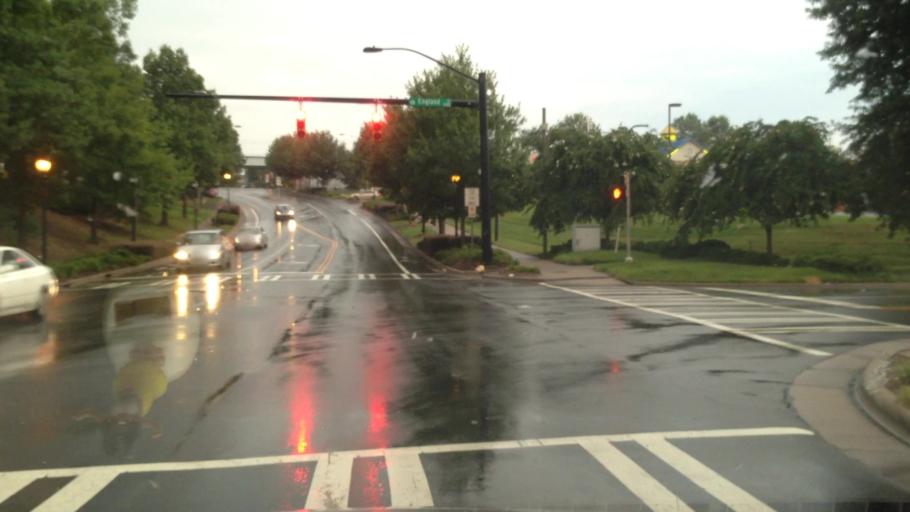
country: US
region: North Carolina
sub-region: Mecklenburg County
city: Pineville
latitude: 35.1378
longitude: -80.8795
